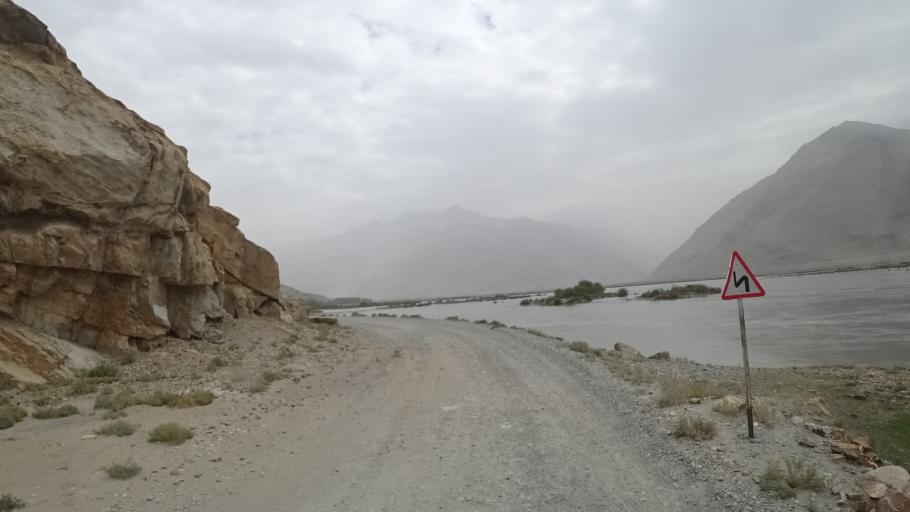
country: AF
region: Badakhshan
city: Khandud
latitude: 37.0250
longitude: 72.6084
